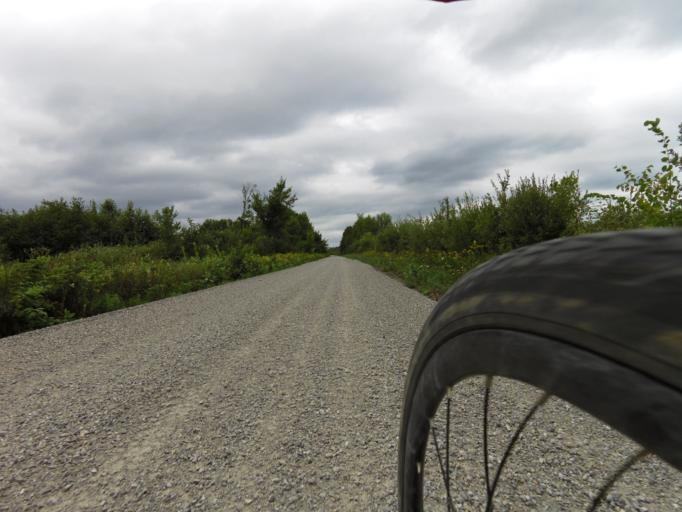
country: CA
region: Ontario
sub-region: Lanark County
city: Smiths Falls
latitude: 44.9511
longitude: -76.0444
